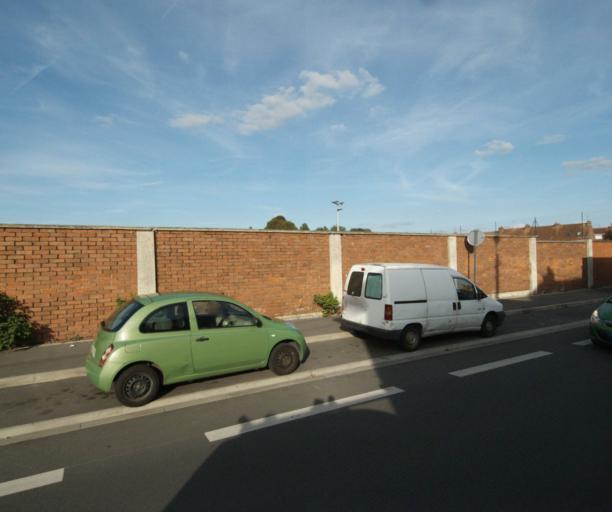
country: FR
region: Nord-Pas-de-Calais
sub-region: Departement du Nord
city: Ronchin
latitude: 50.6090
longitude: 3.0683
